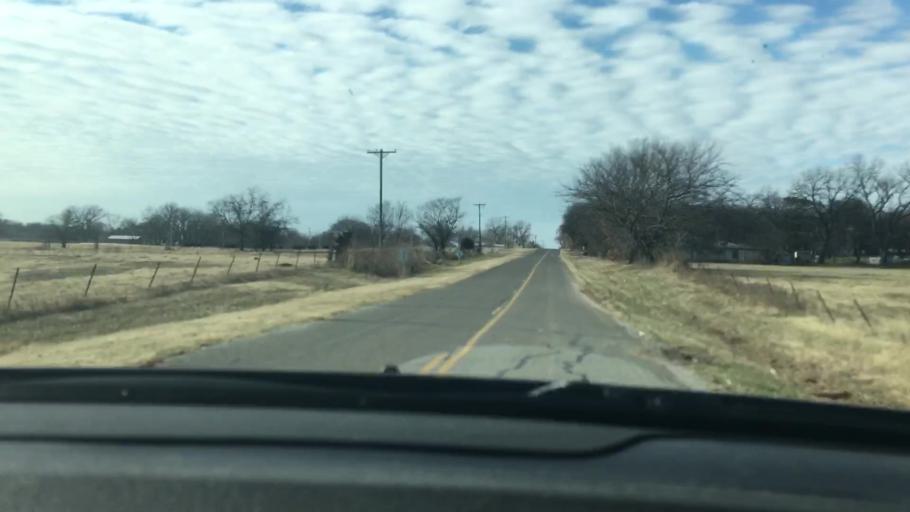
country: US
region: Oklahoma
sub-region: Garvin County
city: Pauls Valley
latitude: 34.7386
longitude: -97.1473
